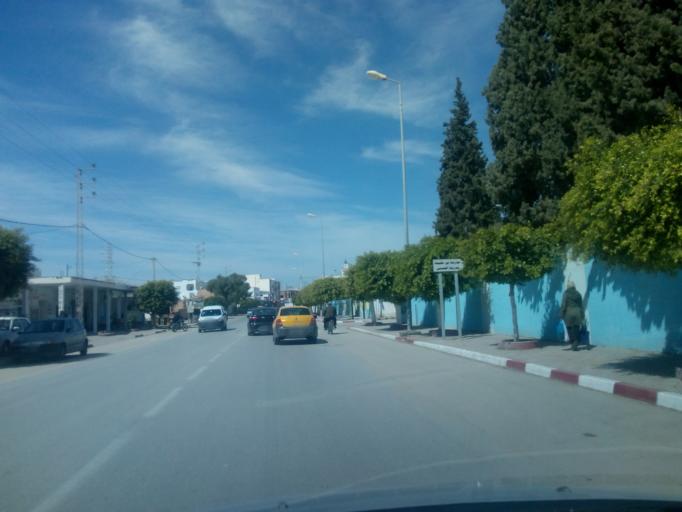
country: TN
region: Safaqis
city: Sfax
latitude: 34.7670
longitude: 10.7095
